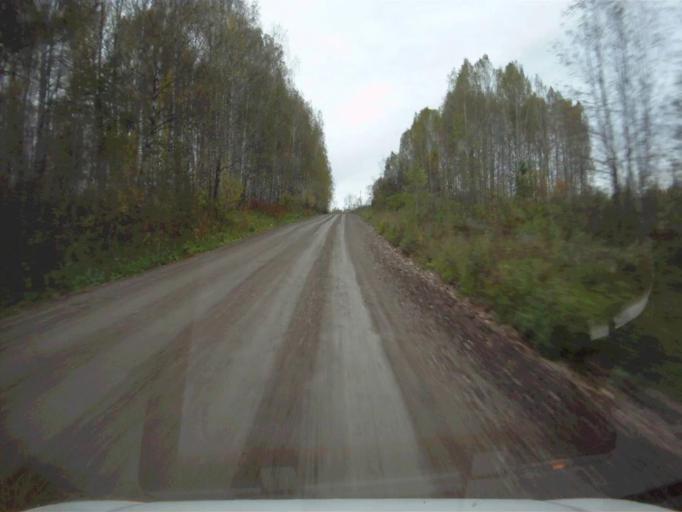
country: RU
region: Chelyabinsk
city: Nyazepetrovsk
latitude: 56.1341
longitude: 59.3100
